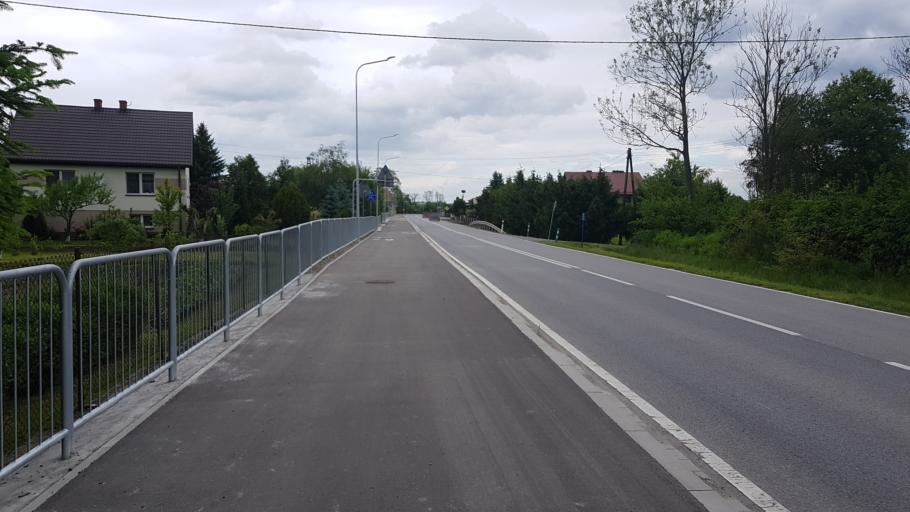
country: PL
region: Lesser Poland Voivodeship
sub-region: Powiat proszowicki
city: Nowe Brzesko
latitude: 50.1120
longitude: 20.3781
